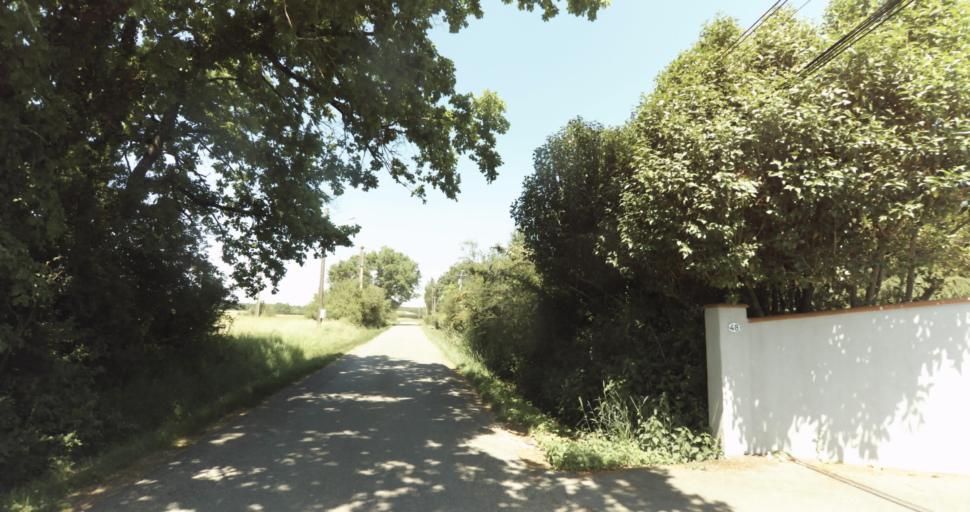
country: FR
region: Midi-Pyrenees
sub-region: Departement de la Haute-Garonne
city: Levignac
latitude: 43.6359
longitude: 1.1877
